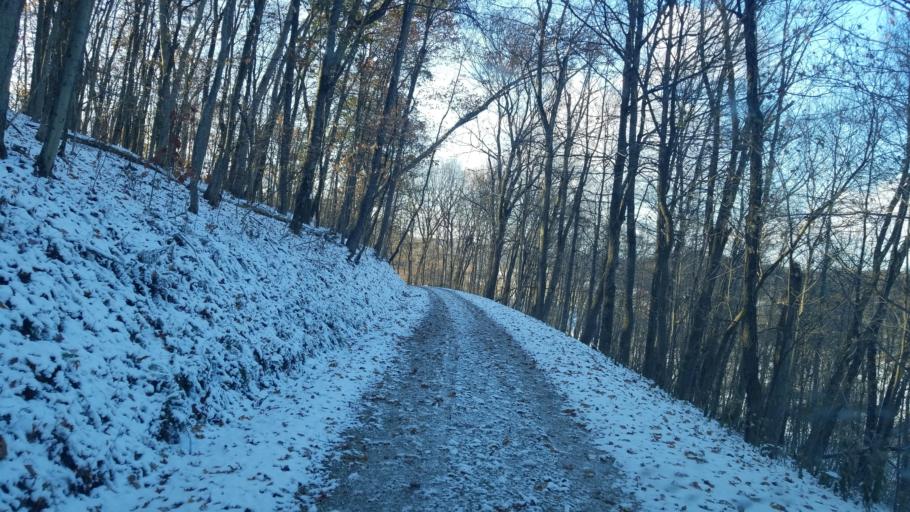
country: US
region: Ohio
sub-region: Licking County
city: Utica
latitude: 40.1625
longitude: -82.3952
